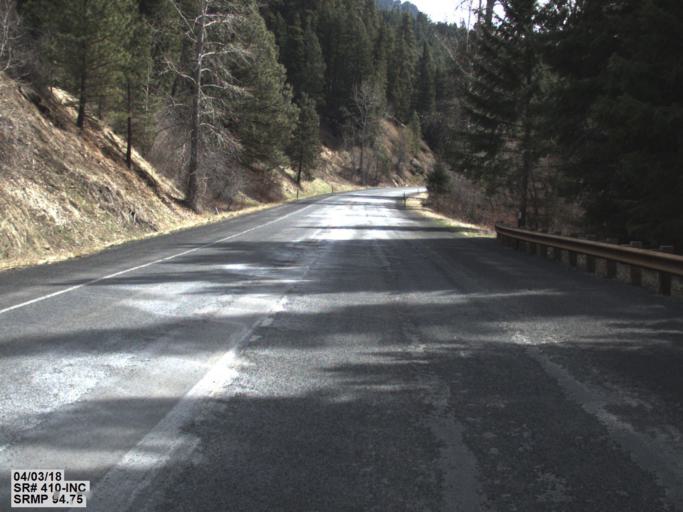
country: US
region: Washington
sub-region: Kittitas County
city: Cle Elum
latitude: 46.9583
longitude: -121.0787
